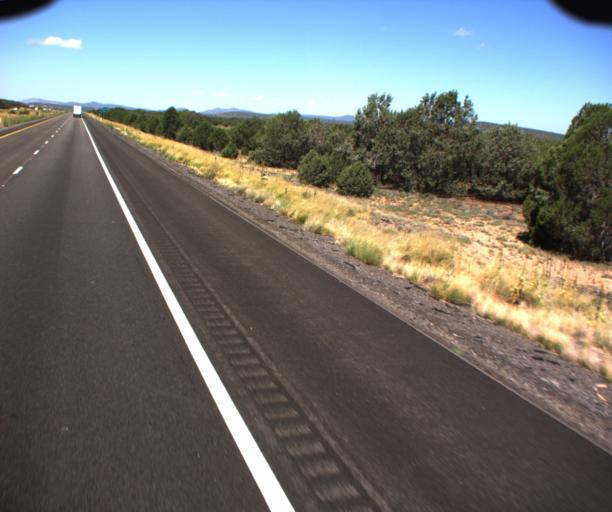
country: US
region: Arizona
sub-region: Mohave County
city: Peach Springs
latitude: 35.1912
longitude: -113.3394
